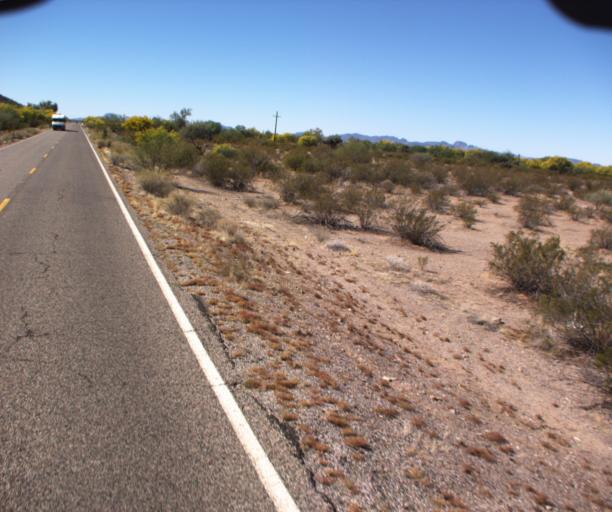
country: US
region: Arizona
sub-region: Pima County
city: Ajo
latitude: 32.2420
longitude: -112.7491
